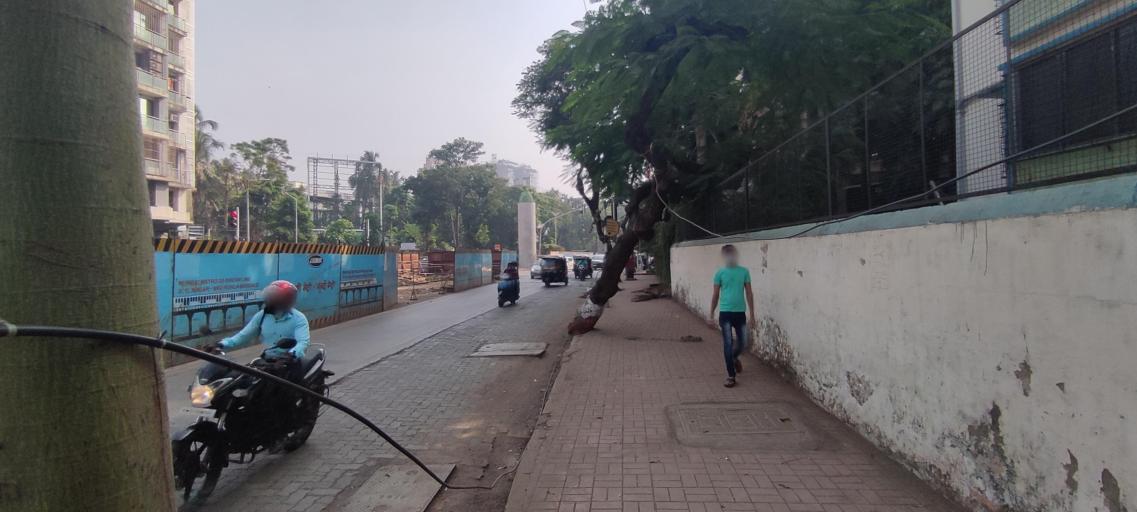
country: IN
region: Maharashtra
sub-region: Mumbai Suburban
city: Mumbai
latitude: 19.1131
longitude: 72.8370
